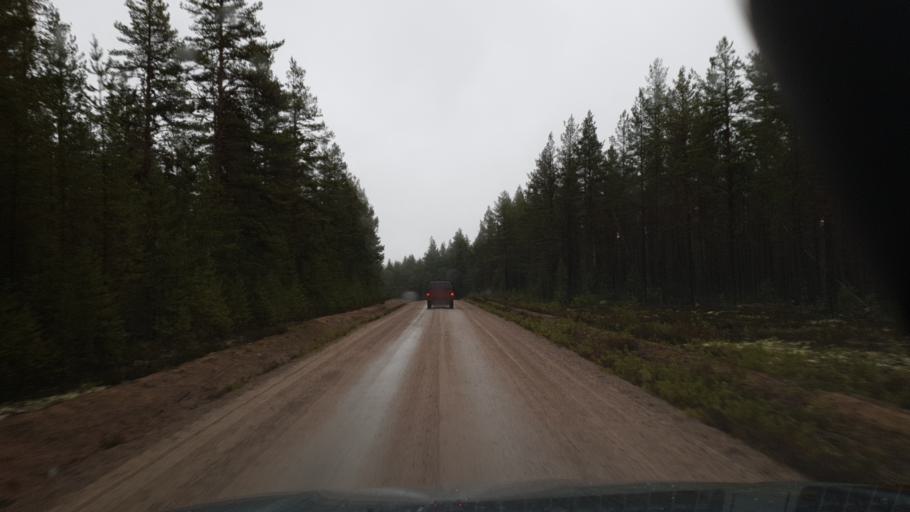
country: SE
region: Vaesternorrland
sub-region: Ange Kommun
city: Ange
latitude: 62.2046
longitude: 15.5520
